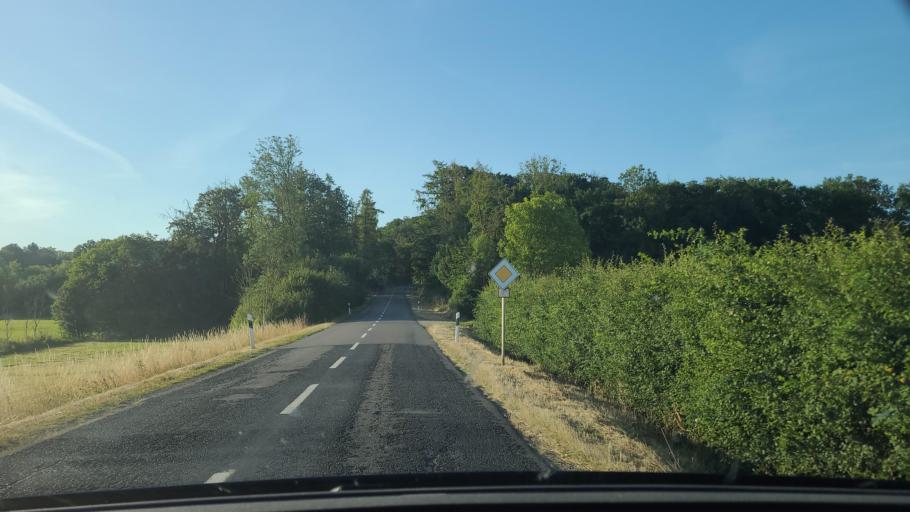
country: LU
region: Luxembourg
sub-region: Canton de Capellen
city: Dippach
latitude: 49.6109
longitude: 5.9904
